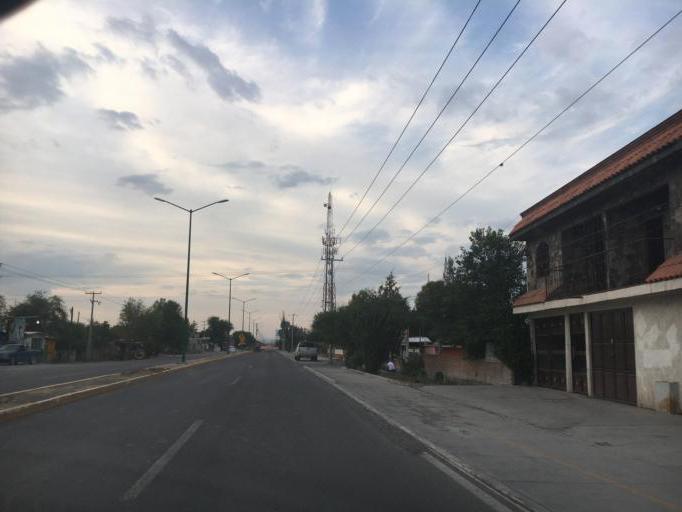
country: MX
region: Guanajuato
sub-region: Leon
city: El CERESO
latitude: 20.9763
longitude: -101.7013
